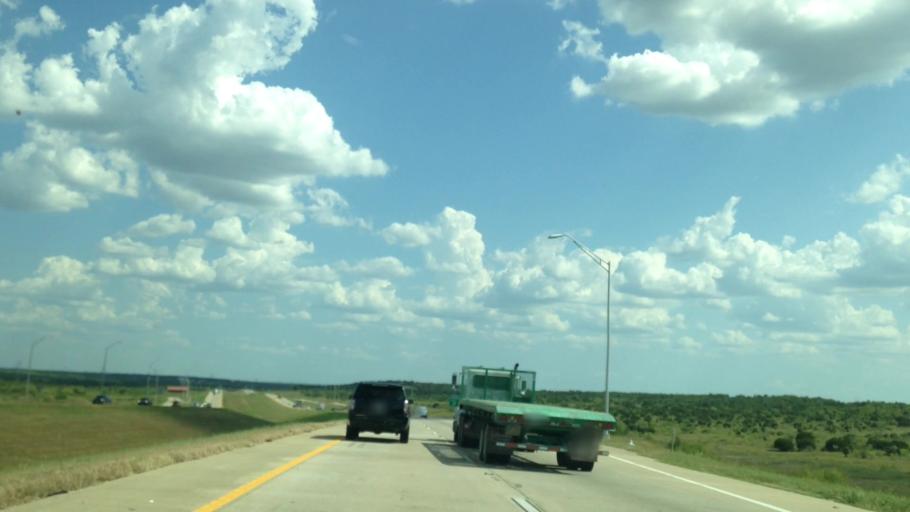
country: US
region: Texas
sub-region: Travis County
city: Manor
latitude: 30.3316
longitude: -97.5866
